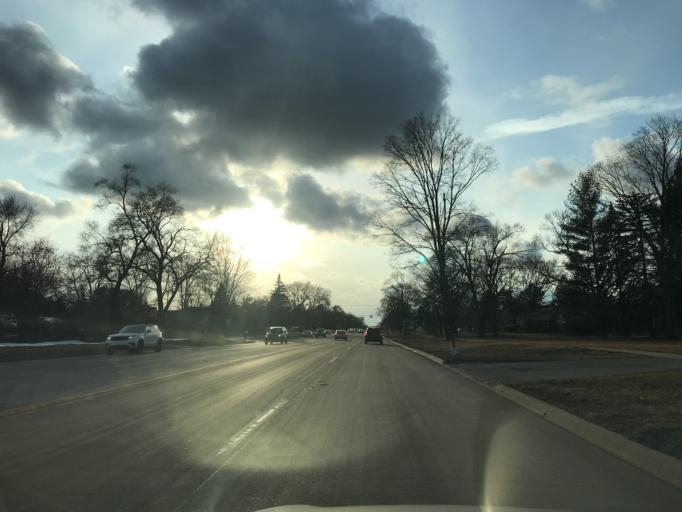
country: US
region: Michigan
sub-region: Oakland County
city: Farmington
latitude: 42.4267
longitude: -83.3523
